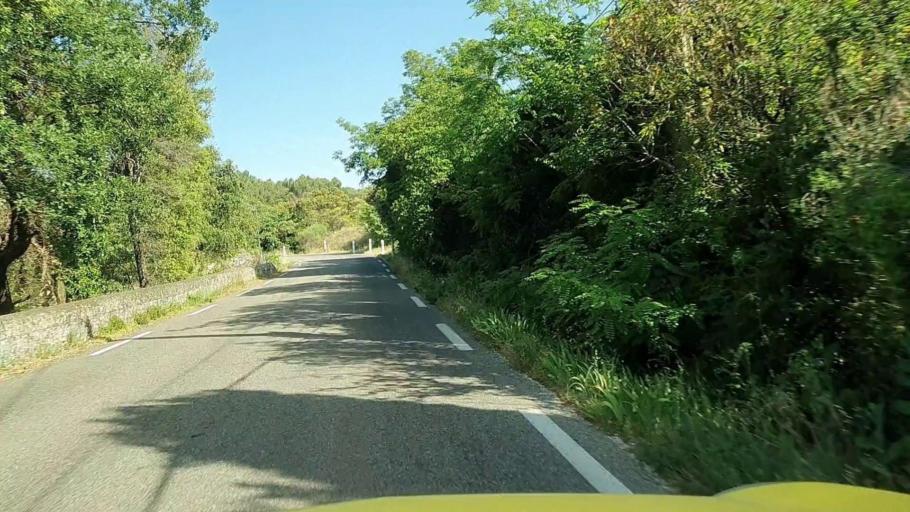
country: FR
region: Languedoc-Roussillon
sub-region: Departement du Gard
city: Montaren-et-Saint-Mediers
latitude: 44.0600
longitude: 4.3981
